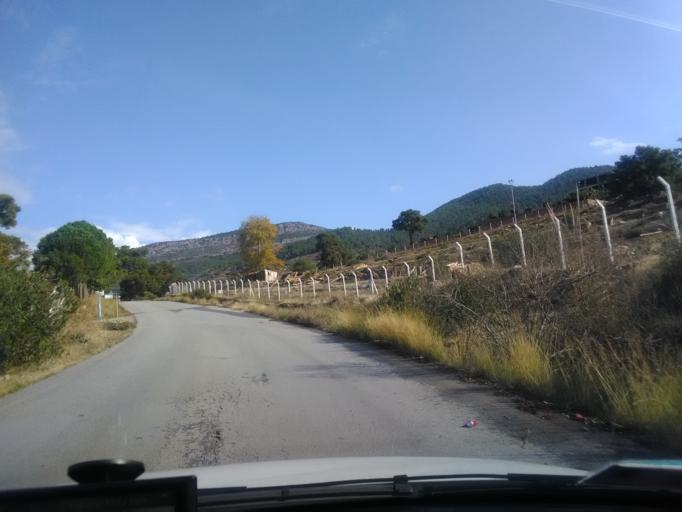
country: TR
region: Antalya
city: Gazipasa
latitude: 36.2969
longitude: 32.3347
